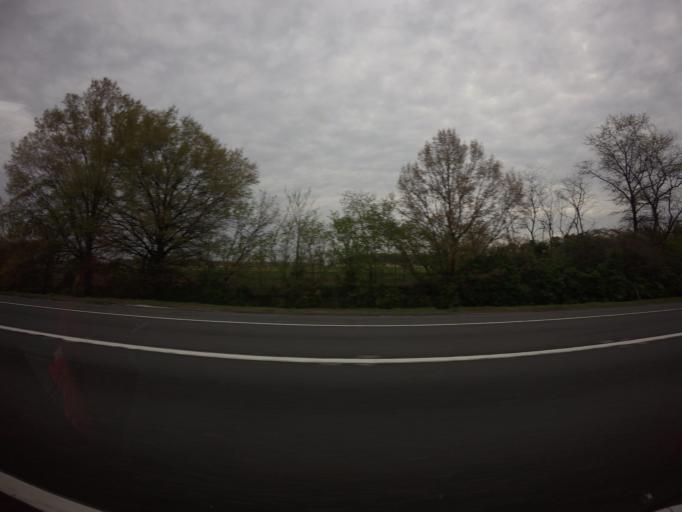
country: US
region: Maryland
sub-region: Frederick County
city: Linganore
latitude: 39.3737
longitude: -77.2255
